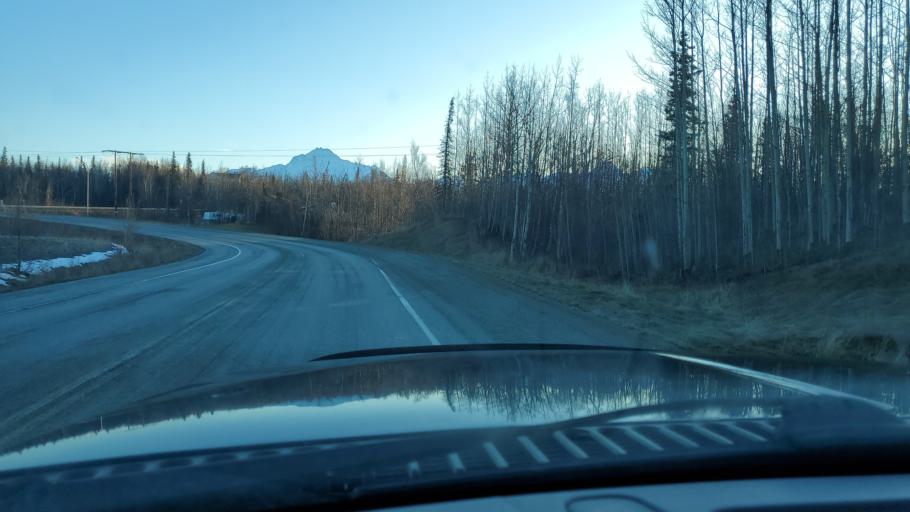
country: US
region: Alaska
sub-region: Matanuska-Susitna Borough
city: Gateway
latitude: 61.5932
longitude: -149.2420
